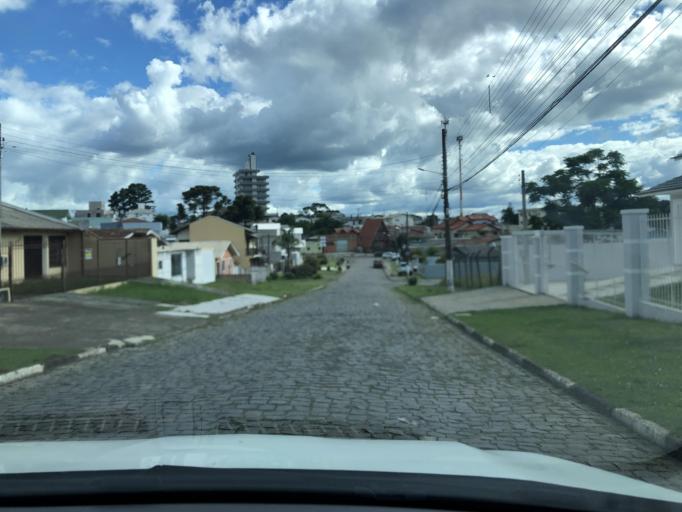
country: BR
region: Santa Catarina
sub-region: Lages
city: Lages
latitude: -27.8216
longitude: -50.3088
